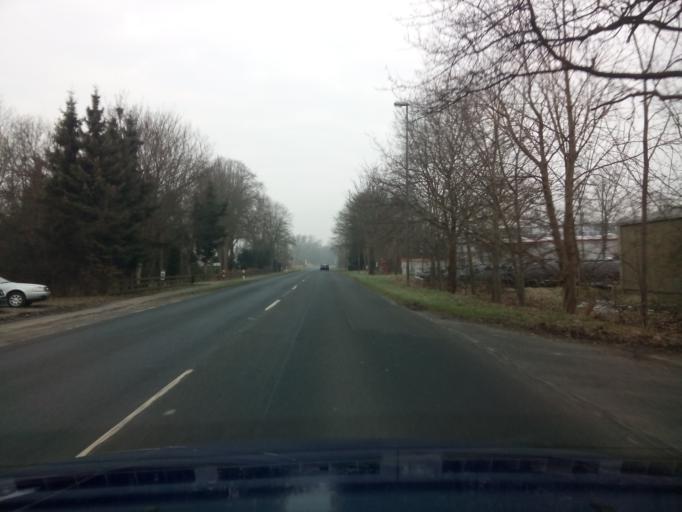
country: DE
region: Lower Saxony
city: Loxstedt
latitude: 53.4571
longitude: 8.6064
